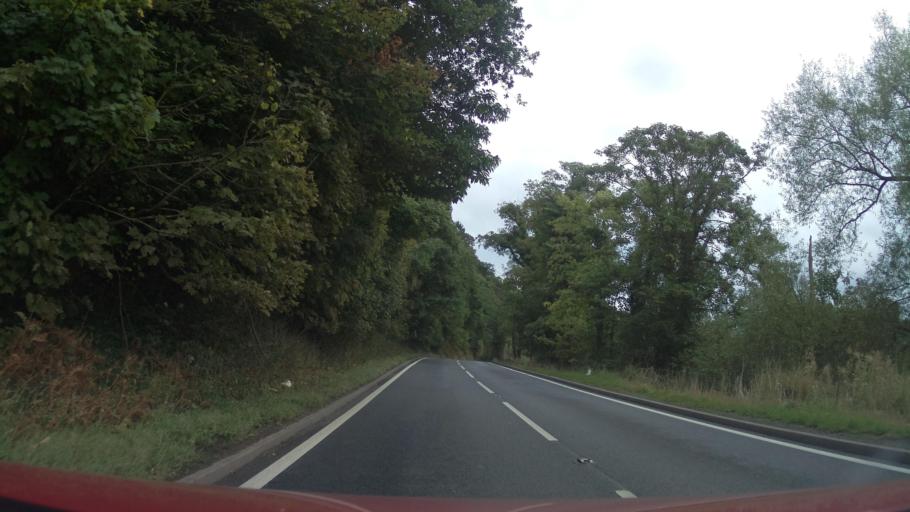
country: GB
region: England
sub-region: Shropshire
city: Bridgnorth
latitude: 52.5492
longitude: -2.4069
